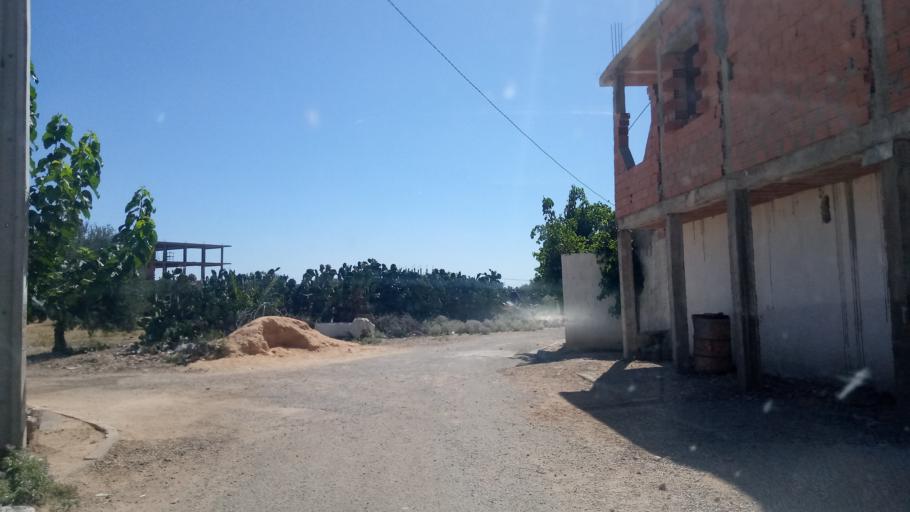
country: TN
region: Al Qayrawan
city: Sbikha
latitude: 36.1300
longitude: 10.0901
